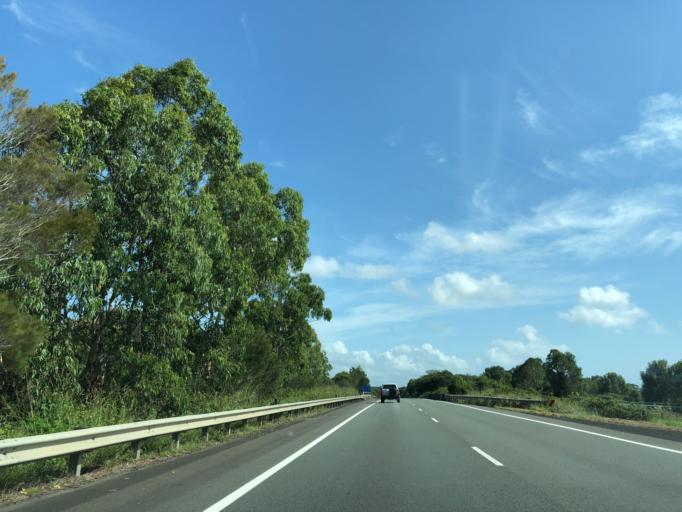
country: AU
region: New South Wales
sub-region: Byron Shire
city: Brunswick Heads
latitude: -28.6052
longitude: 153.5459
